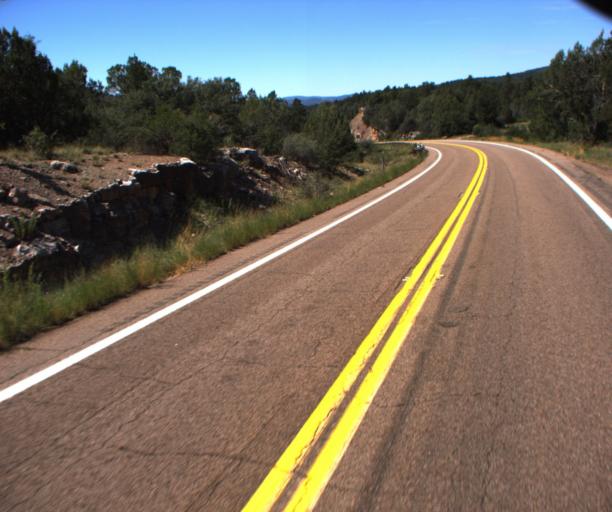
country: US
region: Arizona
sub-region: Navajo County
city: Cibecue
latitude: 33.8658
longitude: -110.4119
